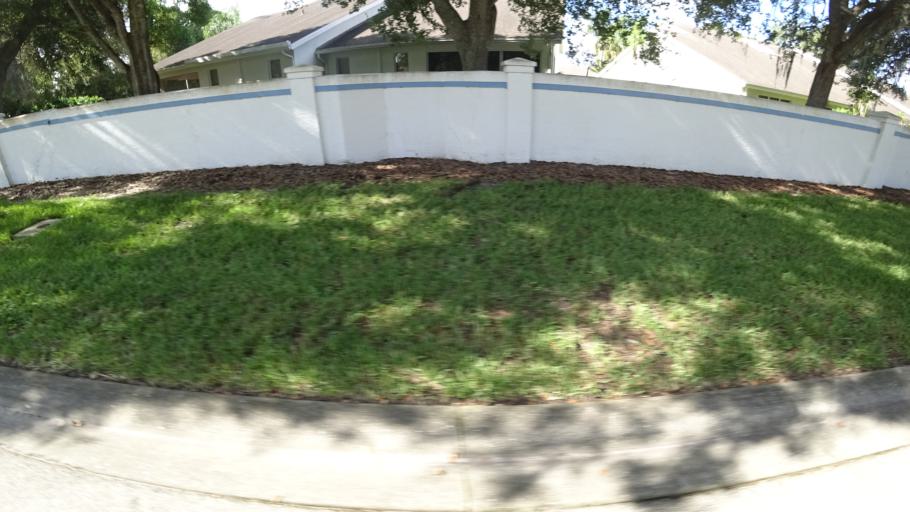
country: US
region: Florida
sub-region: Sarasota County
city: Desoto Lakes
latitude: 27.4005
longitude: -82.4813
